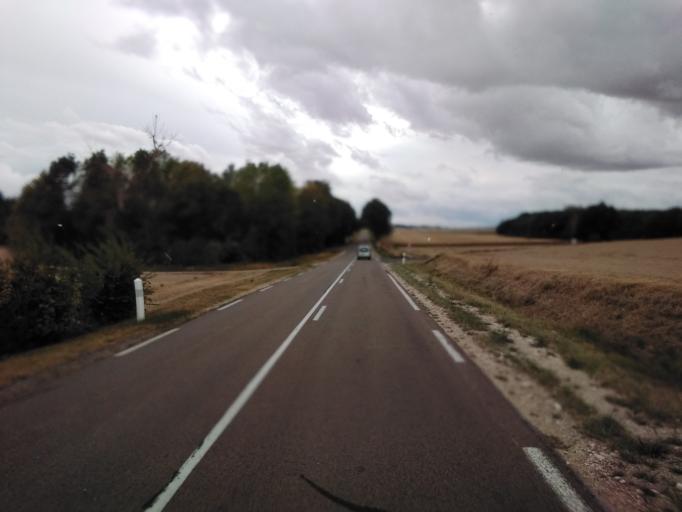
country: FR
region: Champagne-Ardenne
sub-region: Departement de la Marne
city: Frignicourt
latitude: 48.5826
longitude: 4.5394
